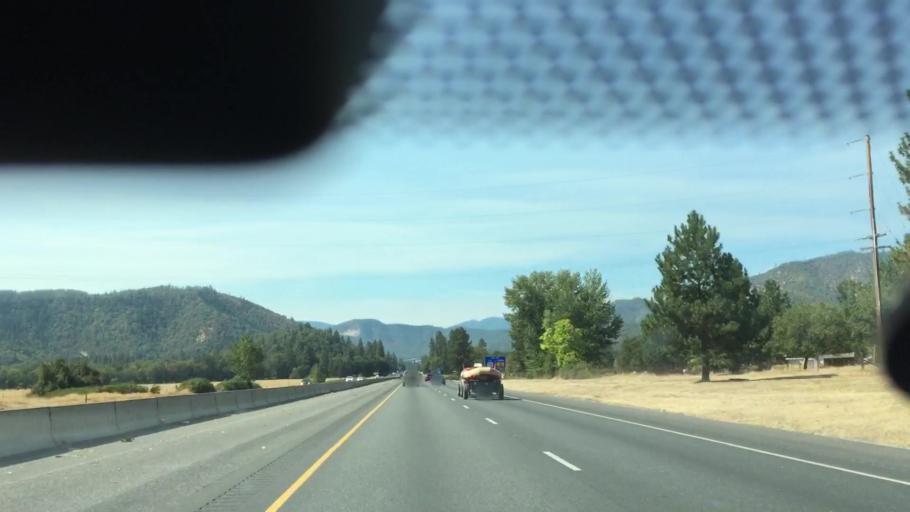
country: US
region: Oregon
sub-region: Jackson County
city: Gold Hill
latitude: 42.4199
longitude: -123.0170
